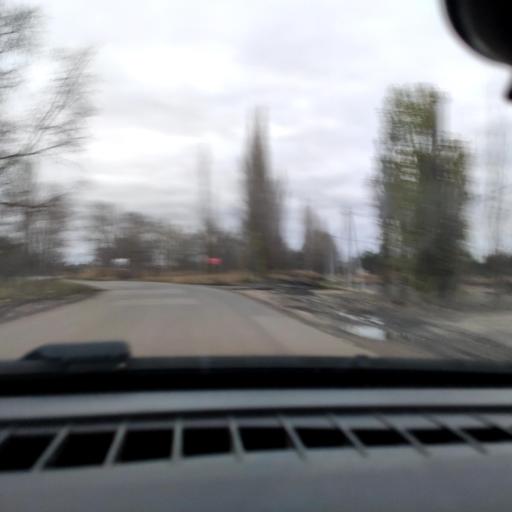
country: RU
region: Voronezj
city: Podgornoye
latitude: 51.8040
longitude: 39.1990
